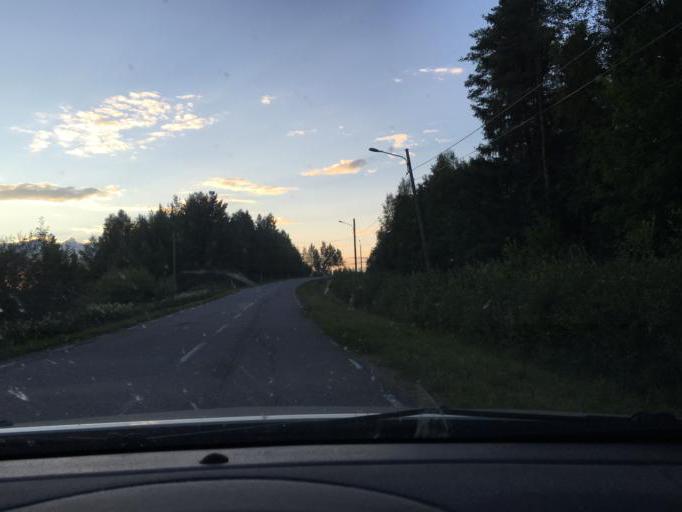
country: SE
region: Norrbotten
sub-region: Kalix Kommun
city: Rolfs
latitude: 65.9036
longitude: 22.9307
